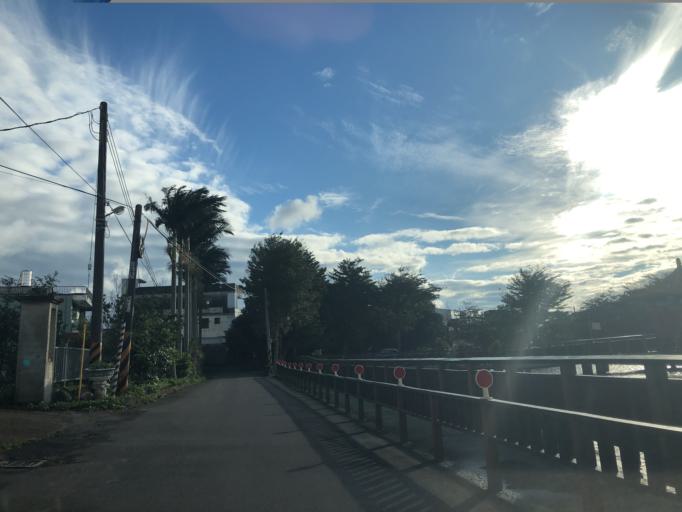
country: TW
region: Taiwan
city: Daxi
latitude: 24.9052
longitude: 121.2665
